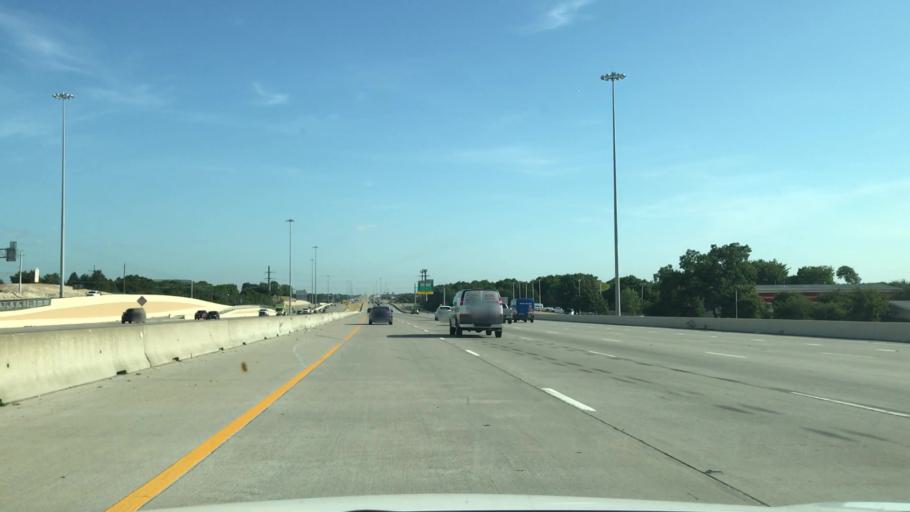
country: US
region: Texas
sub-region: Collin County
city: Fairview
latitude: 33.1749
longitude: -96.6401
